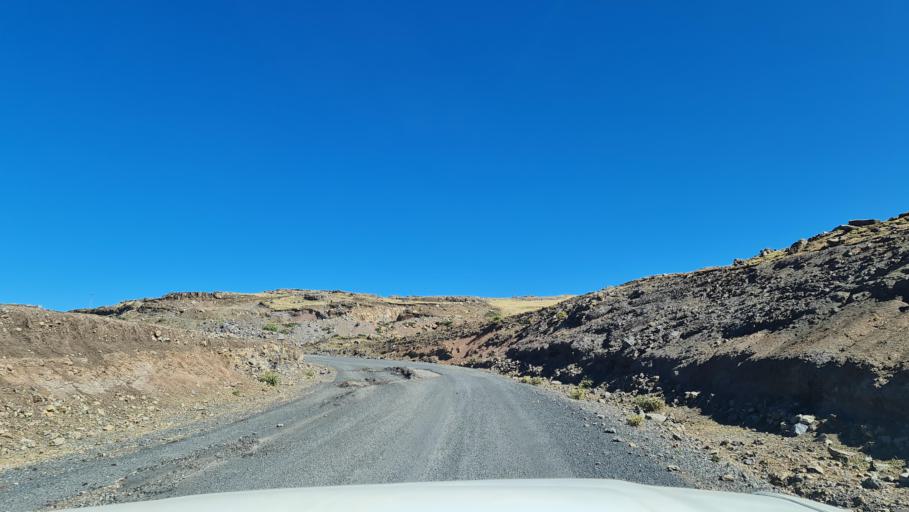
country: ET
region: Amhara
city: Debark'
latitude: 13.1516
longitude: 38.1880
